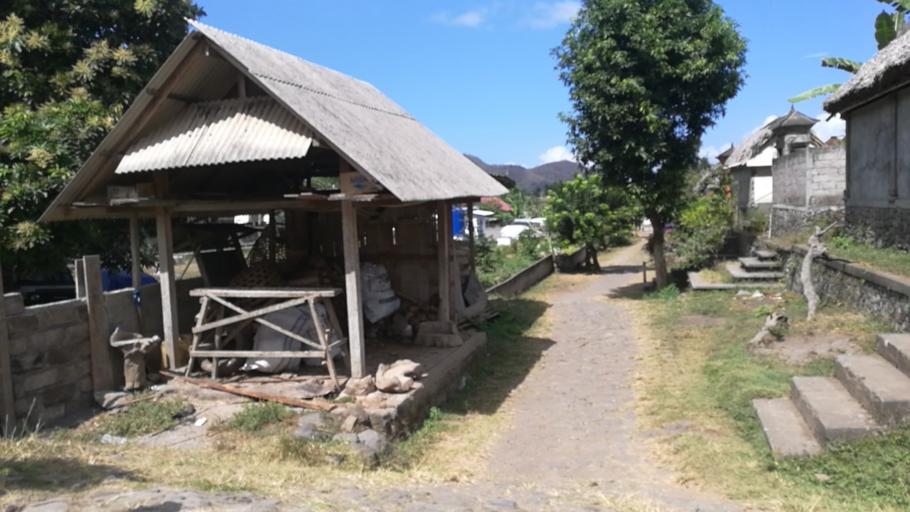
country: ID
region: Bali
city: Banjar Pegeringsingan
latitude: -8.4767
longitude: 115.5667
